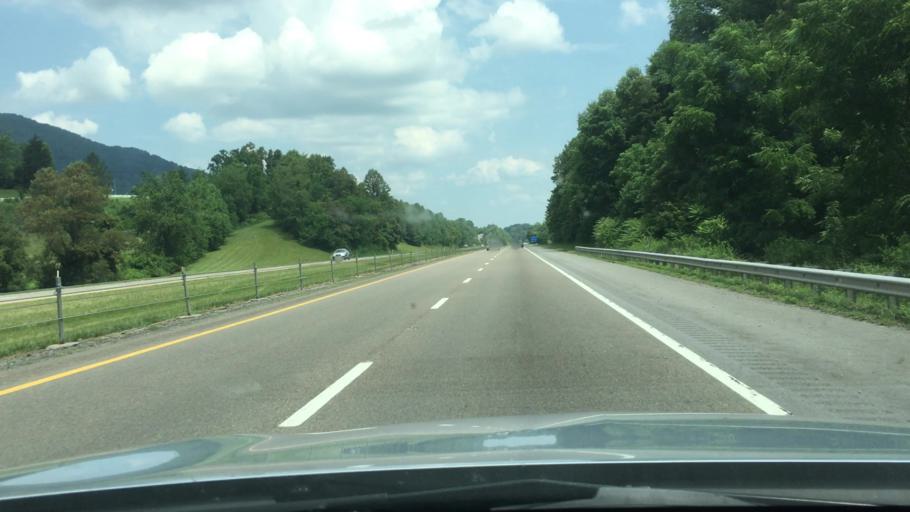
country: US
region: Tennessee
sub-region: Unicoi County
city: Unicoi
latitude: 36.2424
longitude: -82.3266
